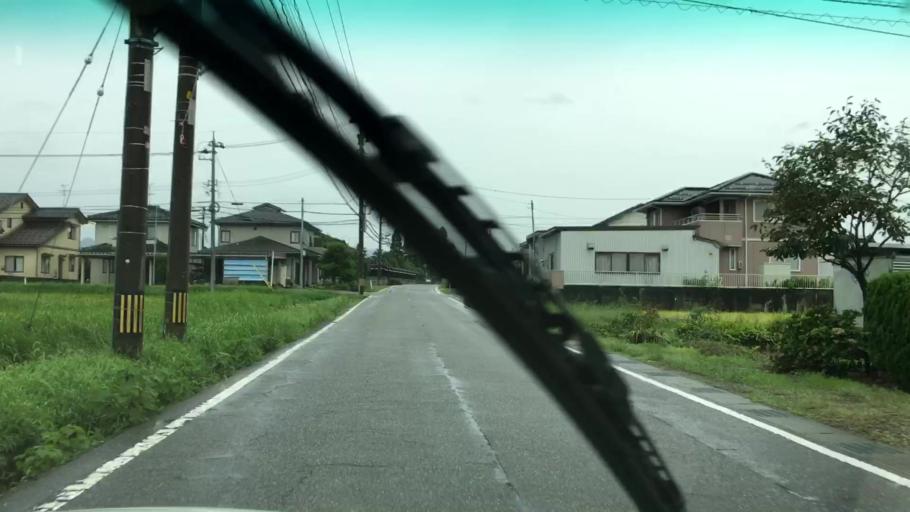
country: JP
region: Toyama
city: Kamiichi
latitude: 36.6424
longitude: 137.3204
